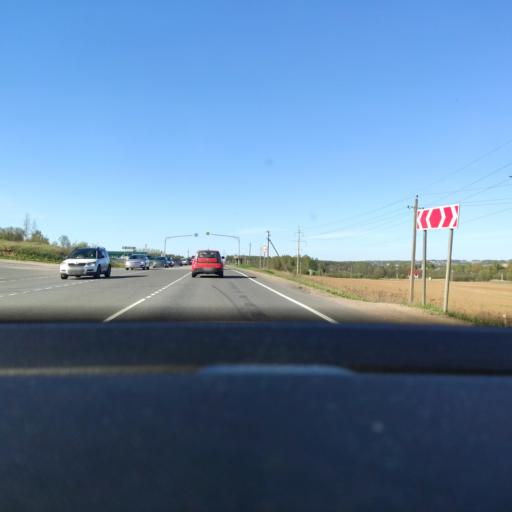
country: RU
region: Moskovskaya
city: Dmitrov
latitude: 56.3443
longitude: 37.4841
